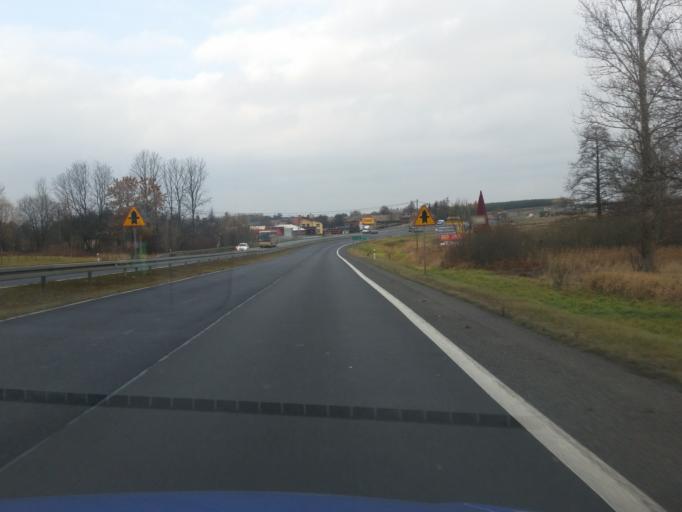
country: PL
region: Silesian Voivodeship
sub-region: Powiat myszkowski
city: Kozieglowy
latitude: 50.5744
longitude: 19.1640
